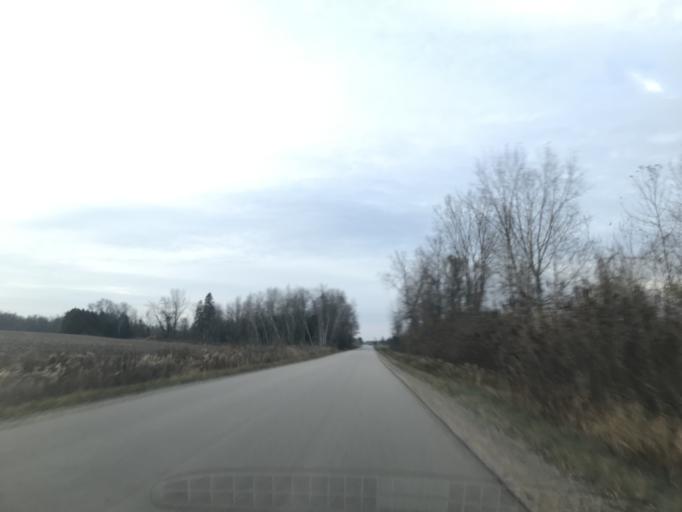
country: US
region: Wisconsin
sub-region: Marinette County
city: Peshtigo
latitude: 45.0886
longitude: -87.7995
